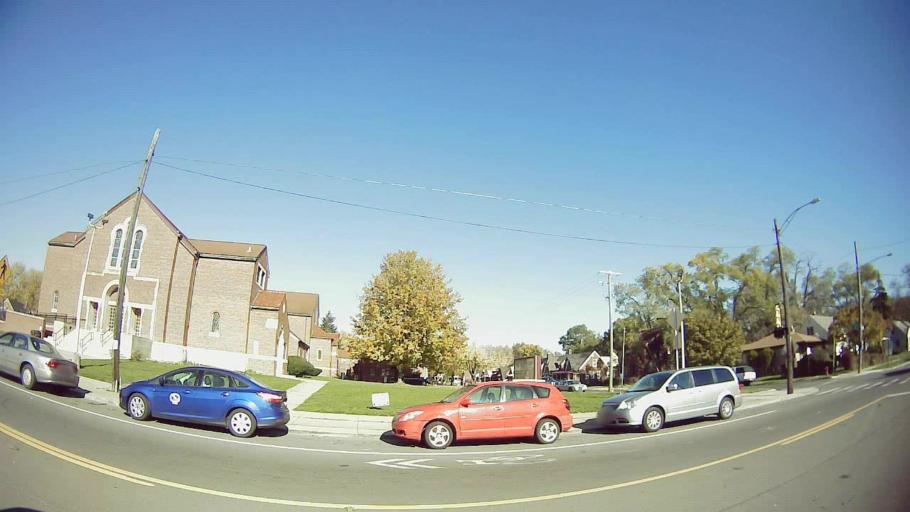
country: US
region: Michigan
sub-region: Wayne County
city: Dearborn
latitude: 42.3653
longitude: -83.2048
